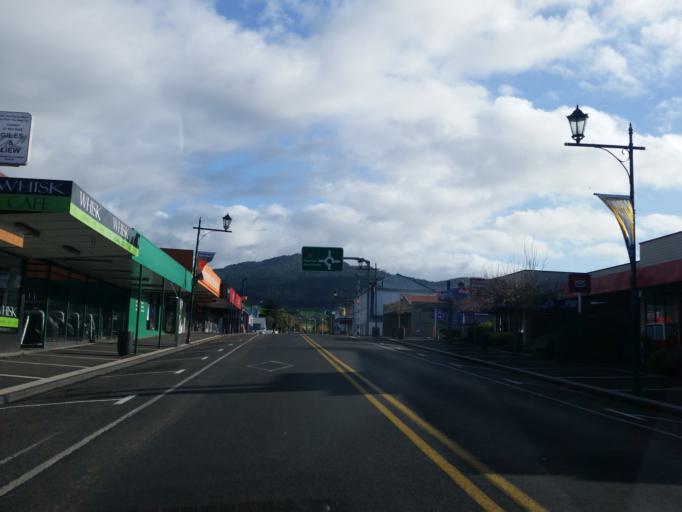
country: NZ
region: Waikato
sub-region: Hauraki District
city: Waihi
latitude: -37.3925
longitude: 175.8412
